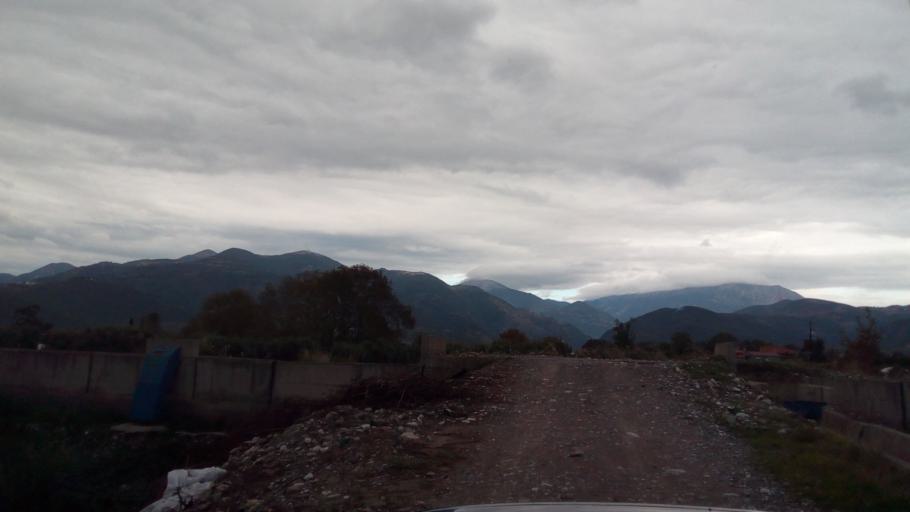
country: GR
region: West Greece
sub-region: Nomos Aitolias kai Akarnanias
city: Nafpaktos
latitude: 38.3879
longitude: 21.8855
